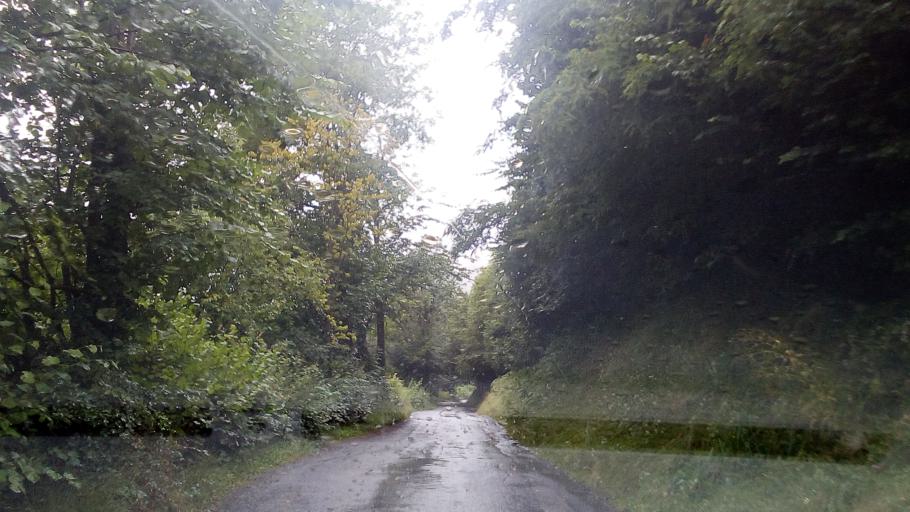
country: FR
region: Midi-Pyrenees
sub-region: Departement des Hautes-Pyrenees
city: Cauterets
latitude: 42.9472
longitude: -0.2214
